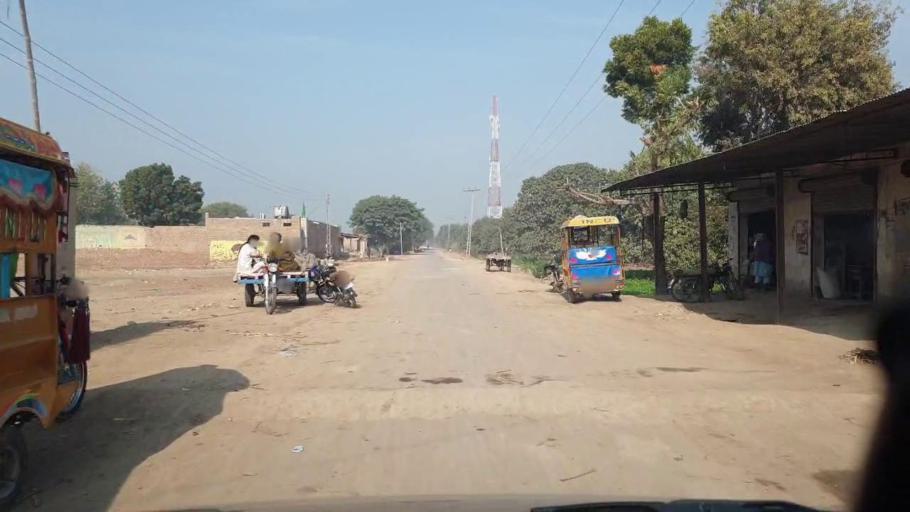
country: PK
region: Sindh
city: Shahdadpur
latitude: 26.0280
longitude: 68.5455
